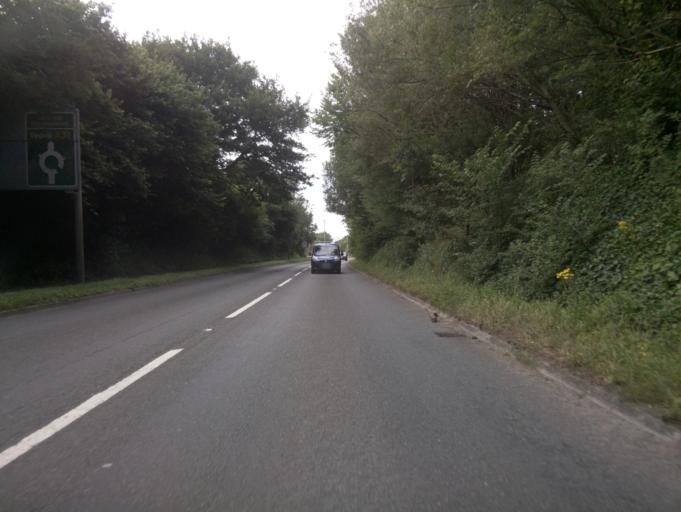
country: GB
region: England
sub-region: Somerset
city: Yeovil
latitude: 50.9210
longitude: -2.6340
